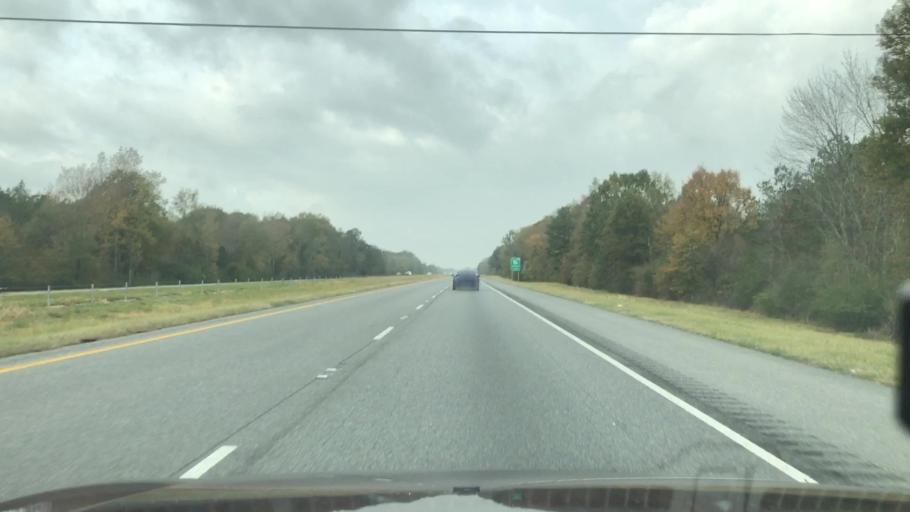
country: US
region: Louisiana
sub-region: Richland Parish
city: Delhi
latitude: 32.4479
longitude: -91.5574
